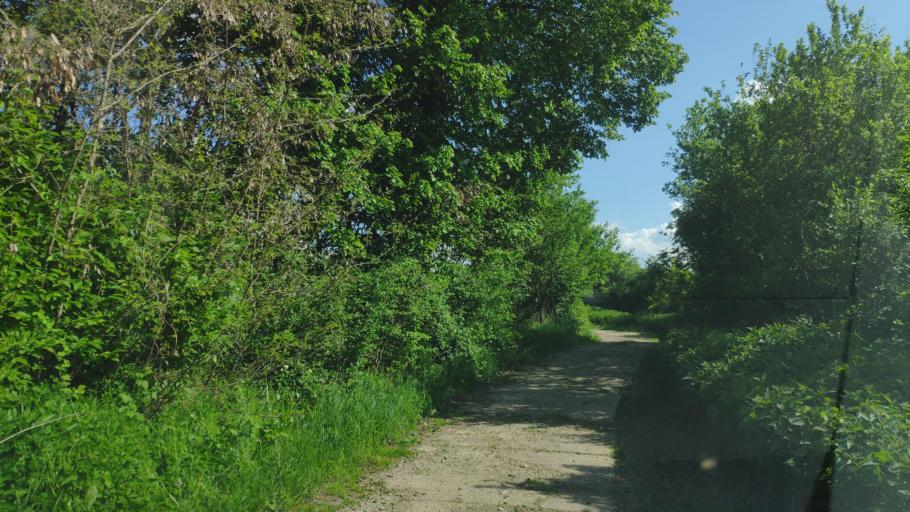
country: SK
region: Presovsky
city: Sabinov
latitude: 49.0450
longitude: 21.1459
